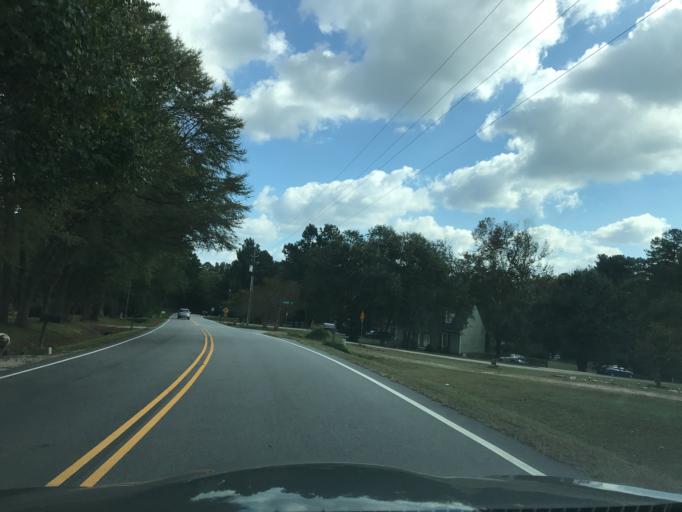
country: US
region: North Carolina
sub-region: Wake County
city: Wake Forest
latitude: 35.9344
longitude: -78.5318
